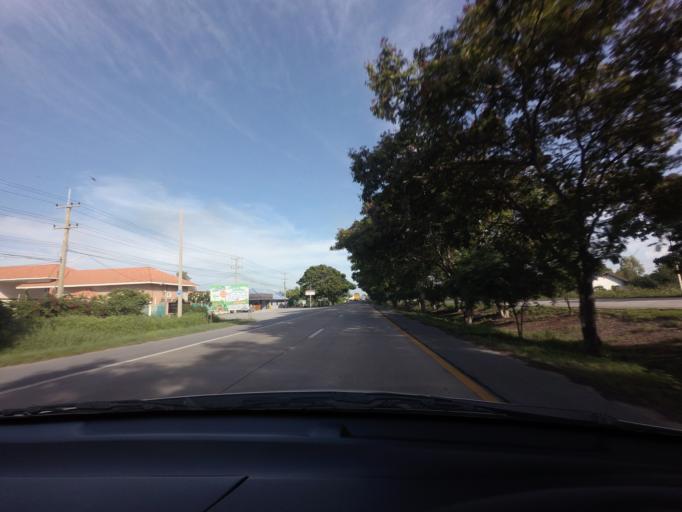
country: TH
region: Phra Nakhon Si Ayutthaya
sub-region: Amphoe Bang Sai
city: Bang Sai
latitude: 14.2864
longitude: 100.2410
